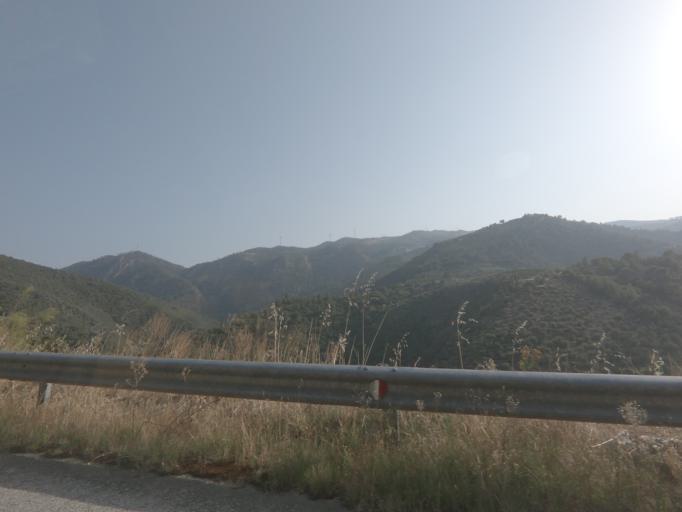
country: PT
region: Viseu
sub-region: Tabuaco
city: Tabuaco
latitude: 41.1254
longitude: -7.5452
